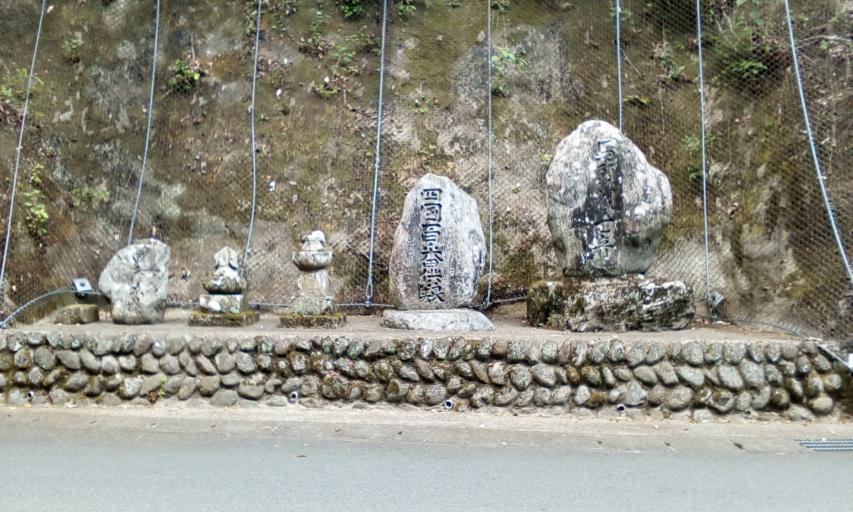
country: JP
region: Tokyo
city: Itsukaichi
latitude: 35.7445
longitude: 139.1248
